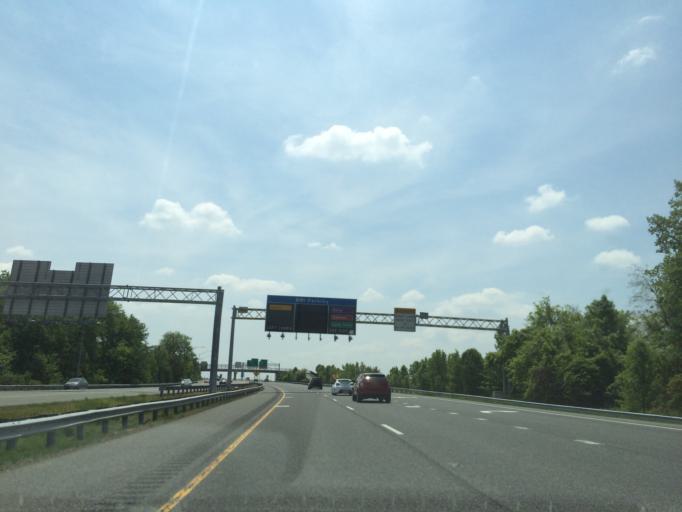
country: US
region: Maryland
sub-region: Howard County
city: Elkridge
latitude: 39.1936
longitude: -76.6886
